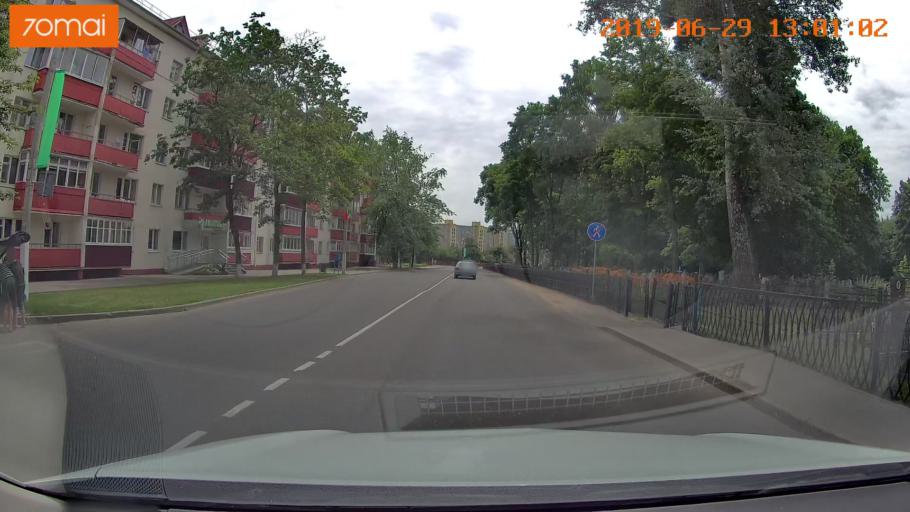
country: BY
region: Minsk
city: Slutsk
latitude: 53.0406
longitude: 27.5590
